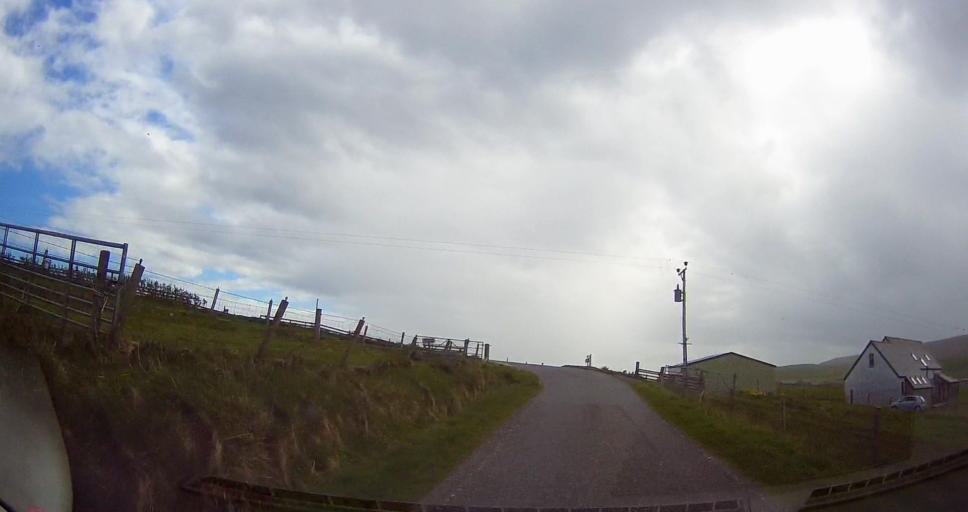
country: GB
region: Scotland
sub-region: Shetland Islands
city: Sandwick
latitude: 59.9167
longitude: -1.3207
